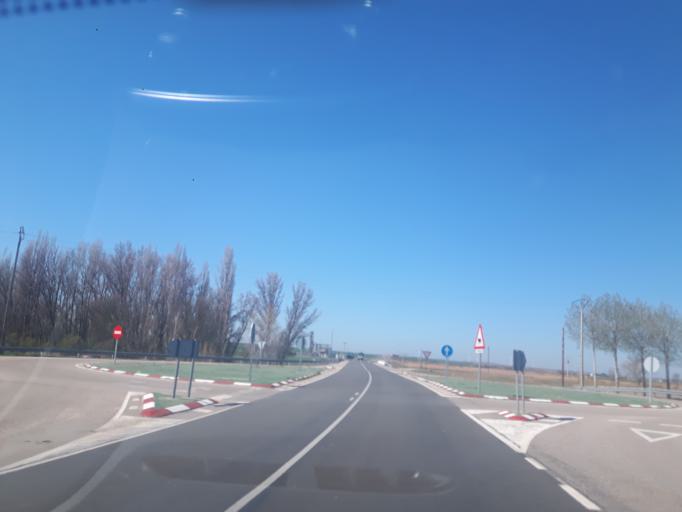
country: ES
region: Castille and Leon
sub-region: Provincia de Salamanca
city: Coca de Alba
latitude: 40.8739
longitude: -5.3666
